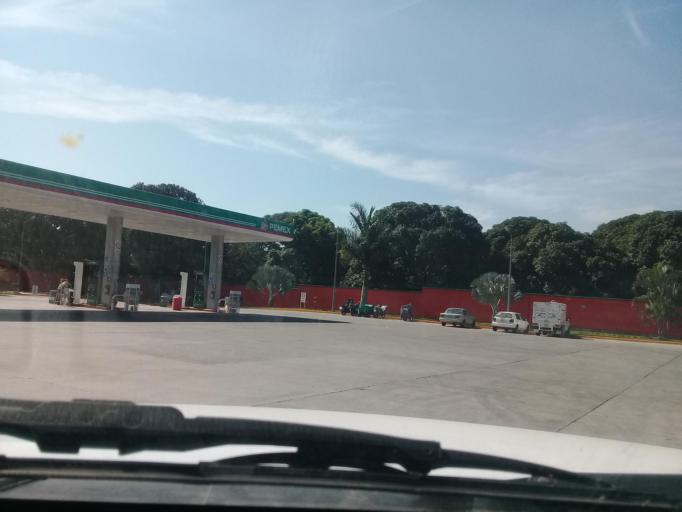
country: MX
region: Veracruz
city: Actopan
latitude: 19.4627
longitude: -96.5741
